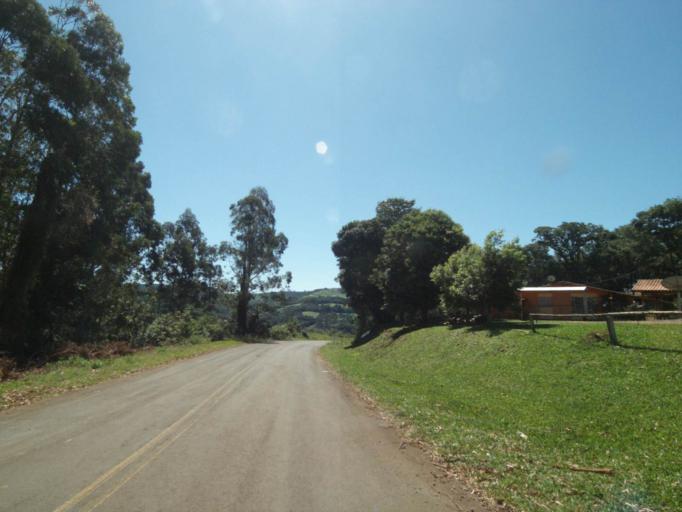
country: AR
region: Misiones
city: Bernardo de Irigoyen
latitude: -26.1887
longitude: -53.3635
